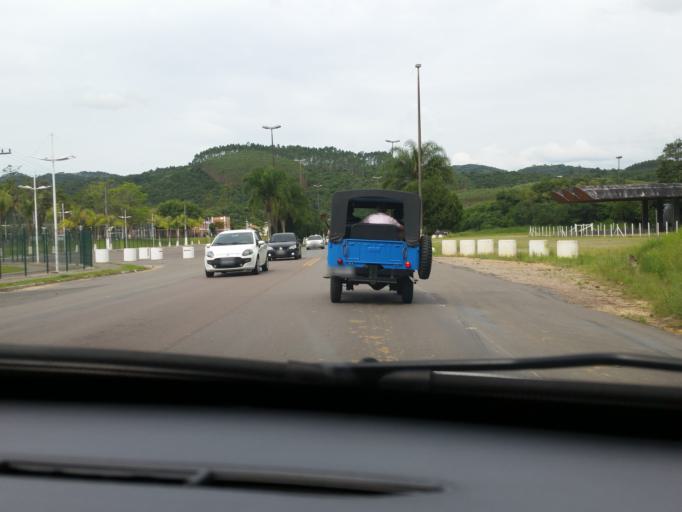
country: BR
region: Santa Catarina
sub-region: Rodeio
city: Gavea
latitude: -27.0265
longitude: -49.3779
